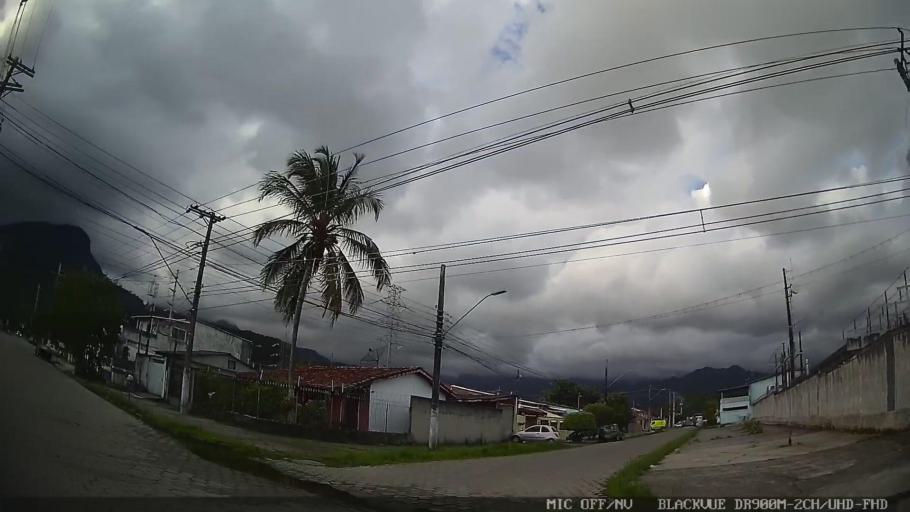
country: BR
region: Sao Paulo
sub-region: Caraguatatuba
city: Caraguatatuba
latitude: -23.6289
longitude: -45.4289
